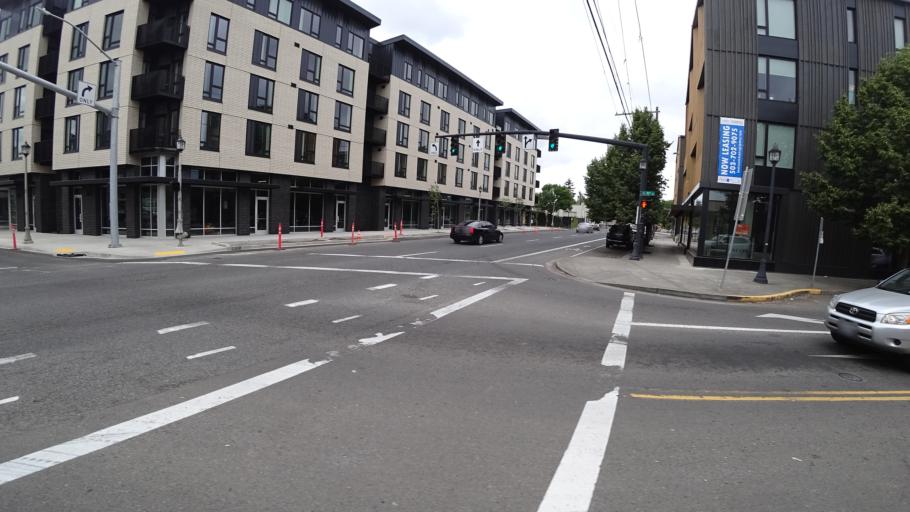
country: US
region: Oregon
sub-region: Multnomah County
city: Lents
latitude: 45.4799
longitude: -122.5686
